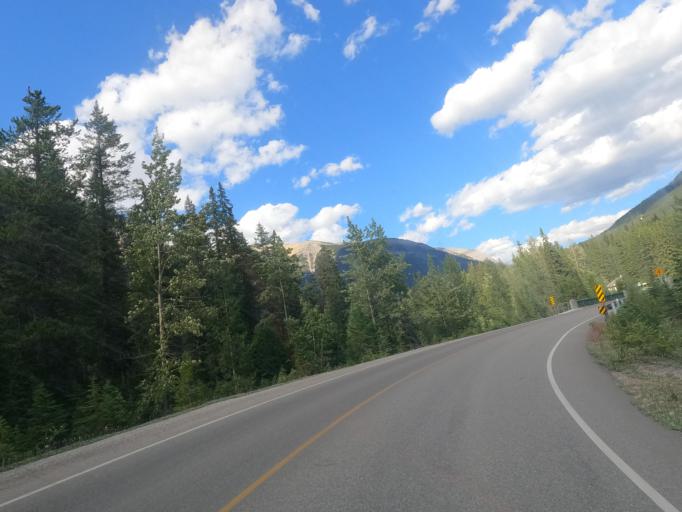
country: CA
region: Alberta
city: Lake Louise
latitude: 51.4226
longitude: -116.4374
